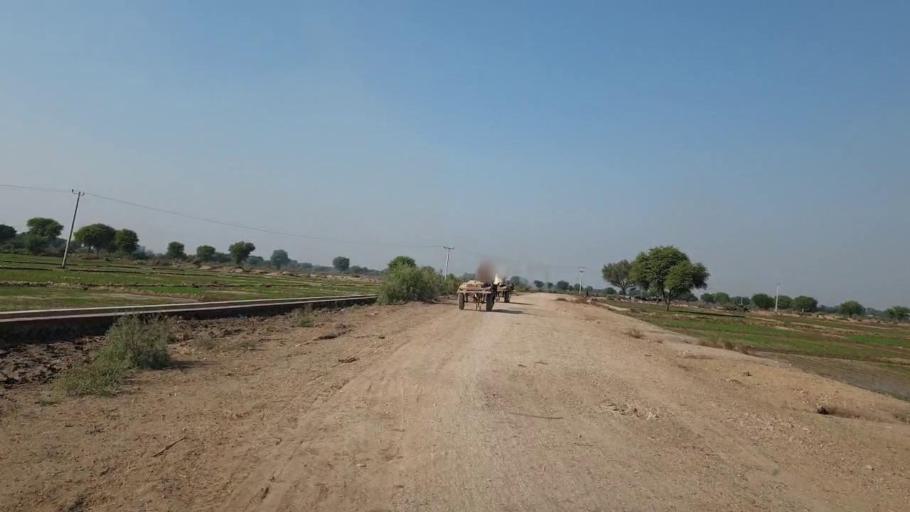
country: PK
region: Sindh
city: Sehwan
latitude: 26.4530
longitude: 67.8157
